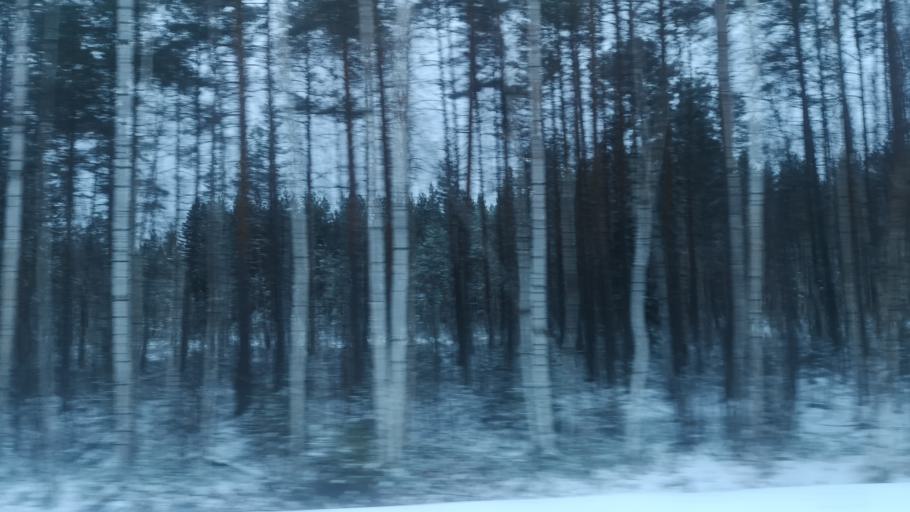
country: FI
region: Southern Savonia
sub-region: Savonlinna
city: Enonkoski
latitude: 62.1078
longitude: 28.6267
